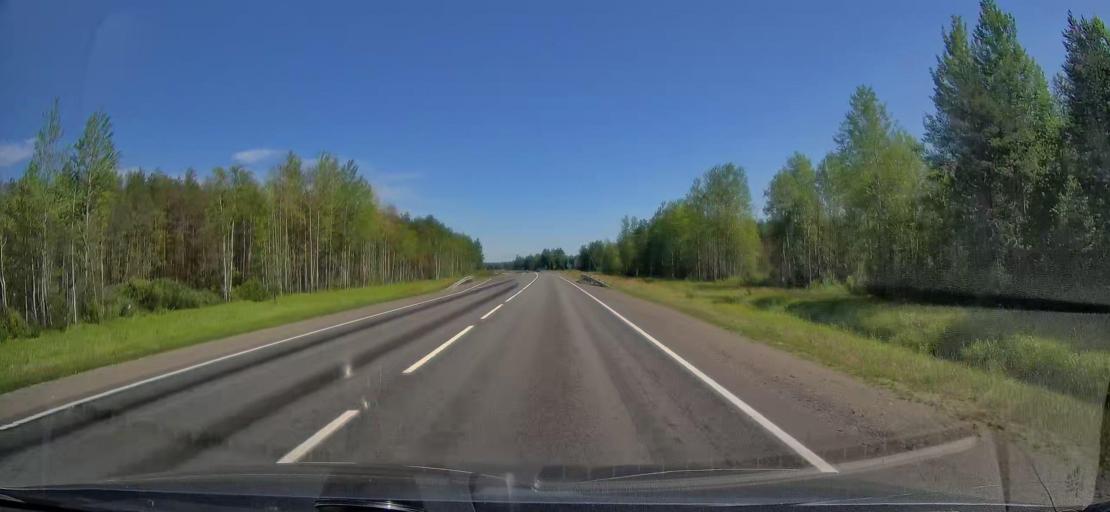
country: RU
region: Tverskaya
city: Ves'yegonsk
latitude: 58.9241
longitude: 37.2376
